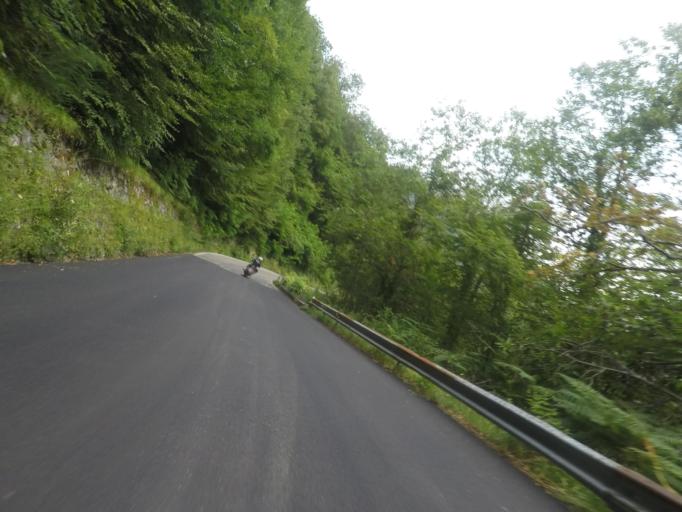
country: IT
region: Tuscany
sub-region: Provincia di Lucca
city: Fontana delle Monache
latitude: 44.0614
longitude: 10.3086
